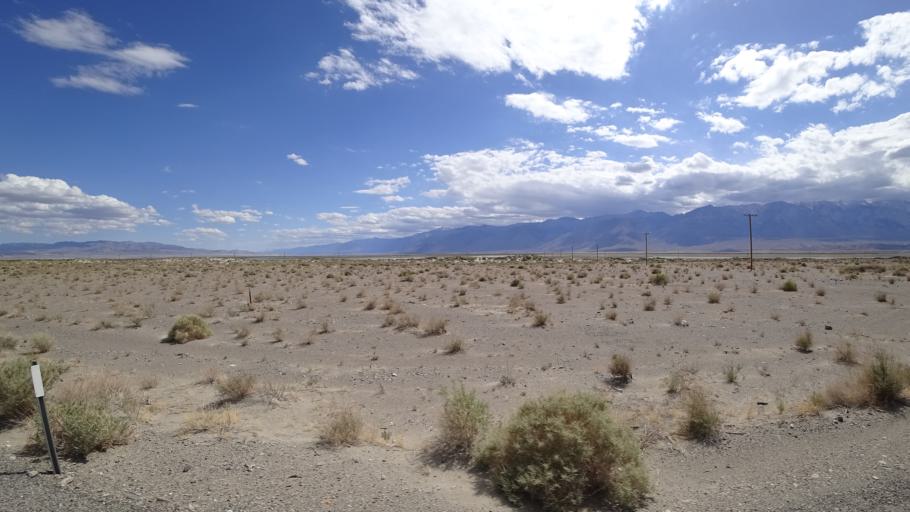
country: US
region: California
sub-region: Inyo County
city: Lone Pine
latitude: 36.5414
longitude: -117.9326
